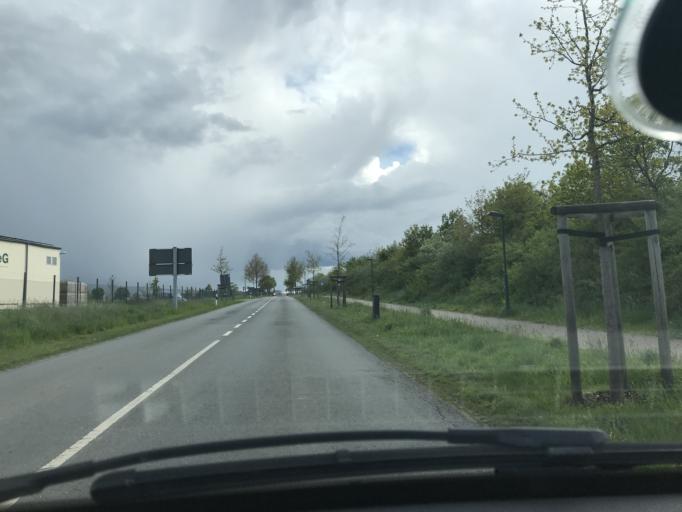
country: DE
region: Lower Saxony
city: Harsefeld
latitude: 53.4471
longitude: 9.5093
